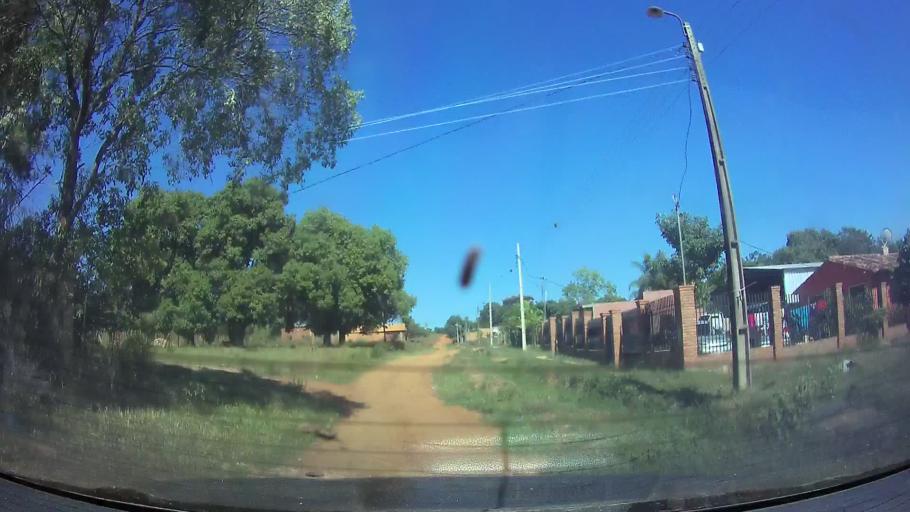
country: PY
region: Central
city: Limpio
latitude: -25.2370
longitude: -57.4500
